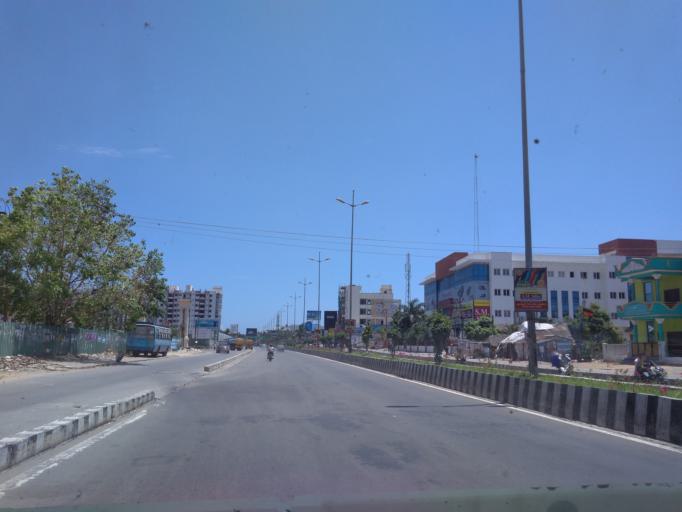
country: IN
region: Tamil Nadu
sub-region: Kancheepuram
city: Injambakkam
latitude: 12.8362
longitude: 80.2285
